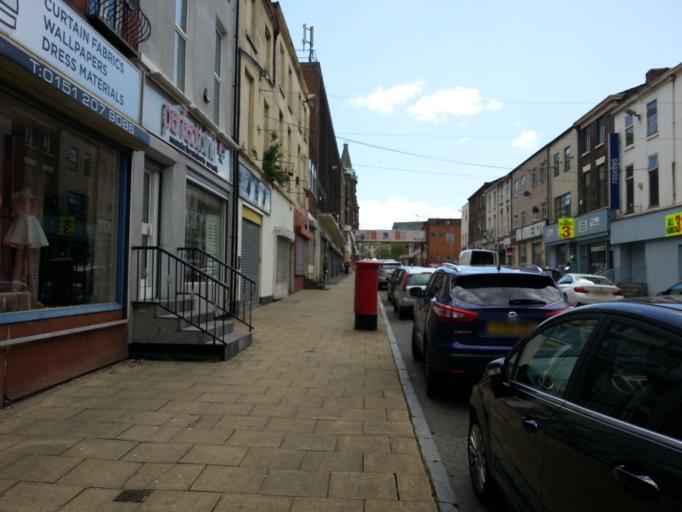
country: GB
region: England
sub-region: Liverpool
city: Liverpool
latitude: 53.4112
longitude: -2.9732
